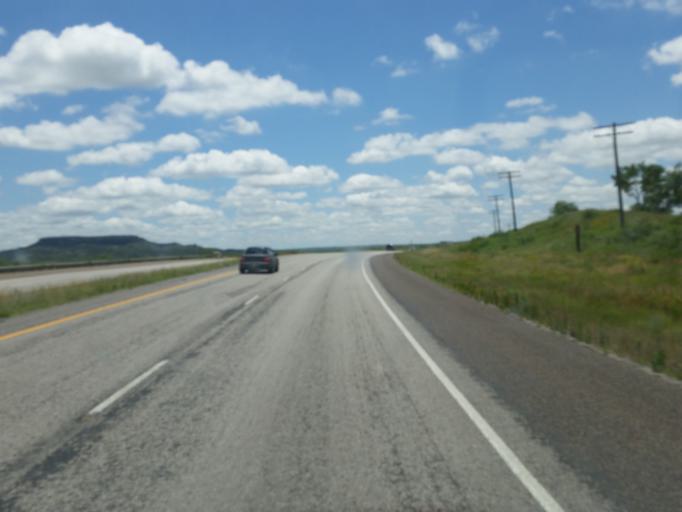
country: US
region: Texas
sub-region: Scurry County
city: Snyder
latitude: 32.9786
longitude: -101.1050
